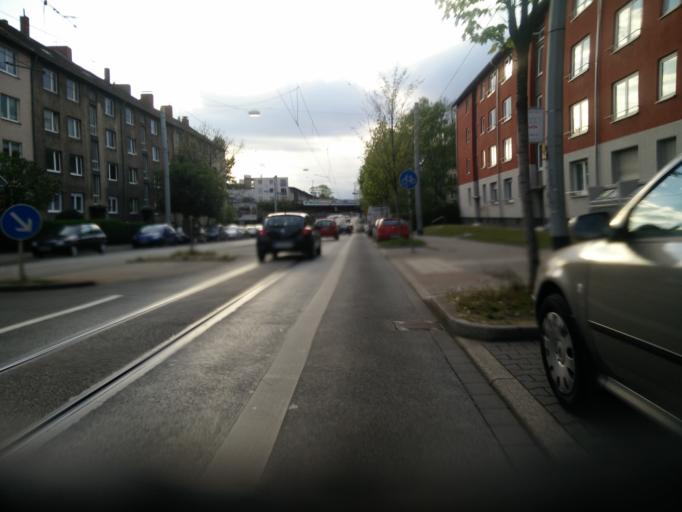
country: DE
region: North Rhine-Westphalia
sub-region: Regierungsbezirk Arnsberg
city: Bochum
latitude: 51.4905
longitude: 7.2031
